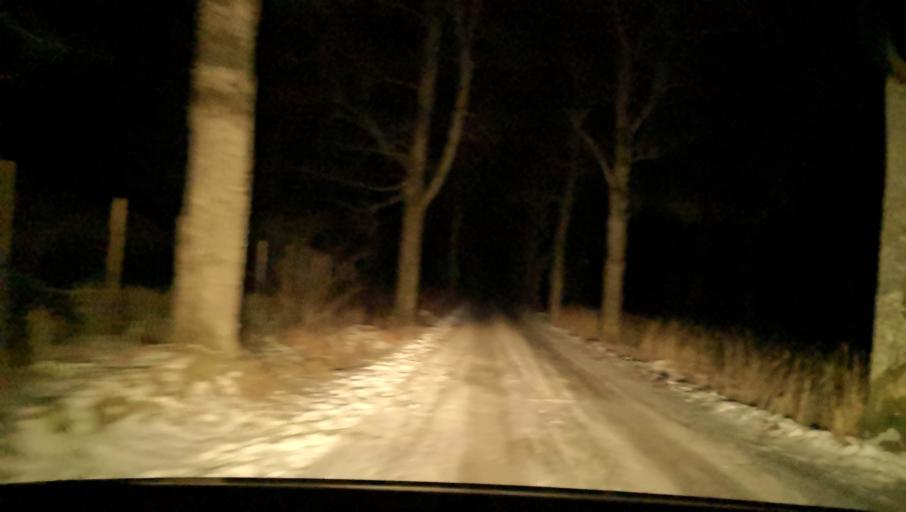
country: SE
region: Stockholm
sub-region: Nacka Kommun
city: Fisksatra
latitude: 59.2750
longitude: 18.2350
